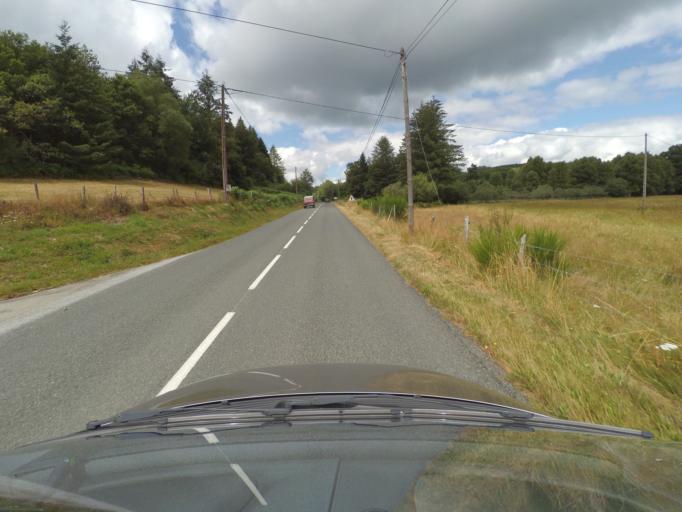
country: FR
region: Limousin
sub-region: Departement de la Haute-Vienne
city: Peyrat-le-Chateau
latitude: 45.8927
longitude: 1.8824
